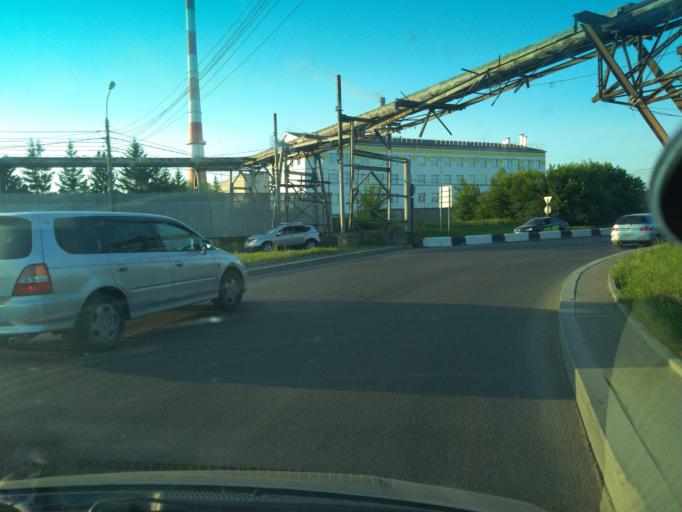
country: RU
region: Krasnoyarskiy
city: Berezovka
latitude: 56.0189
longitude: 93.0311
